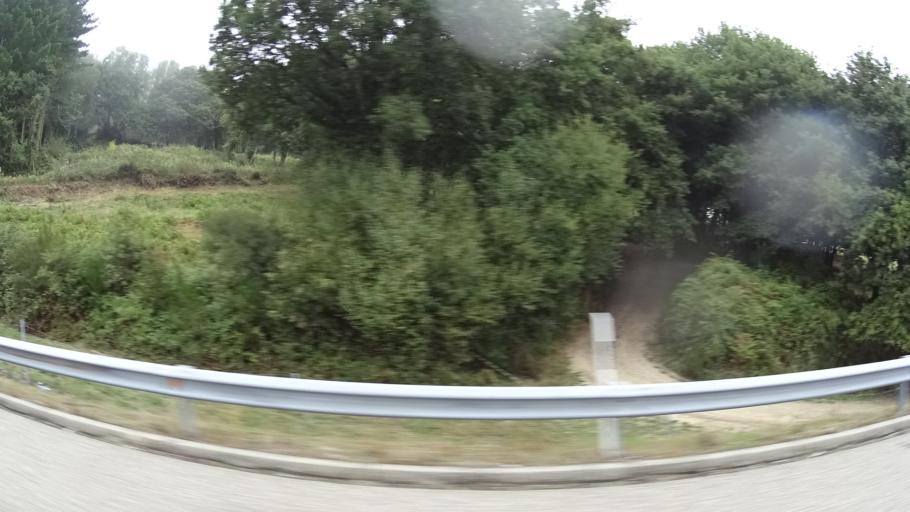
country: ES
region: Galicia
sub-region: Provincia de Lugo
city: Guitiriz
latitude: 43.1794
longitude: -7.8077
